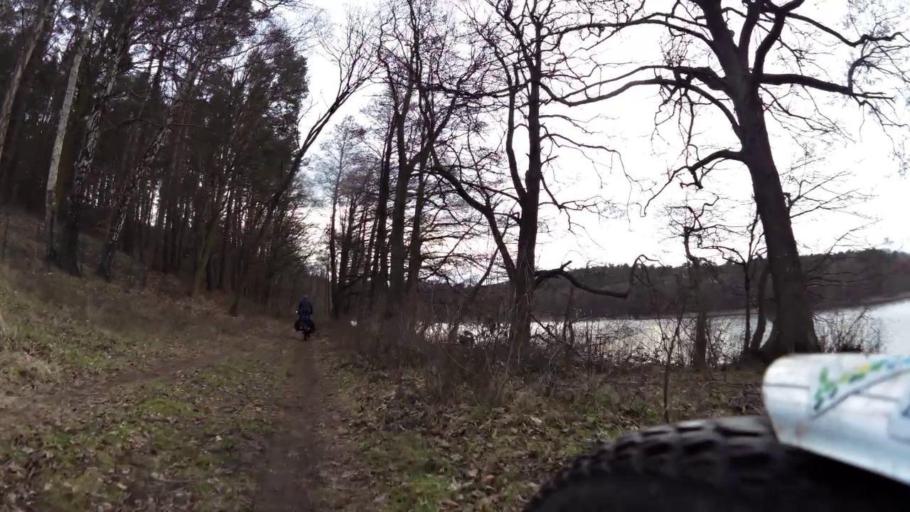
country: PL
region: West Pomeranian Voivodeship
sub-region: Powiat kamienski
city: Wolin
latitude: 53.9580
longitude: 14.5728
